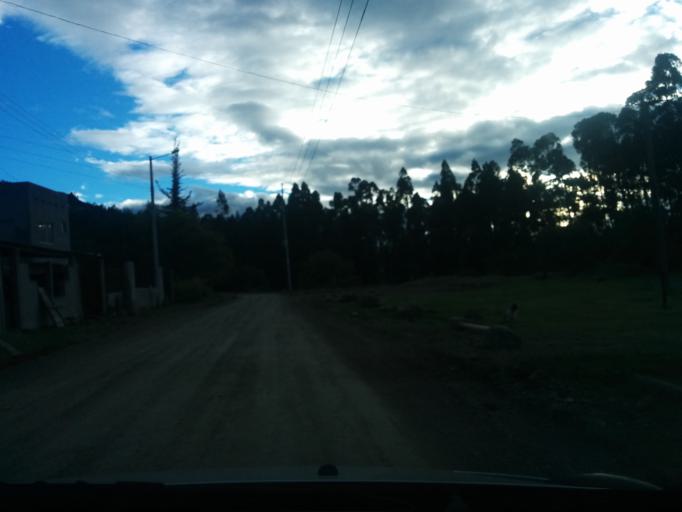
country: EC
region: Azuay
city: Cuenca
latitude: -2.8813
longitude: -78.9469
